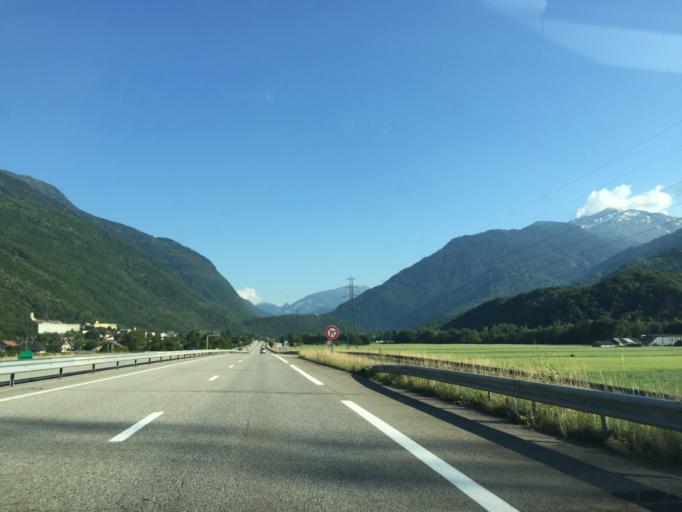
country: FR
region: Rhone-Alpes
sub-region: Departement de la Savoie
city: La Bathie
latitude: 45.6284
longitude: 6.4445
